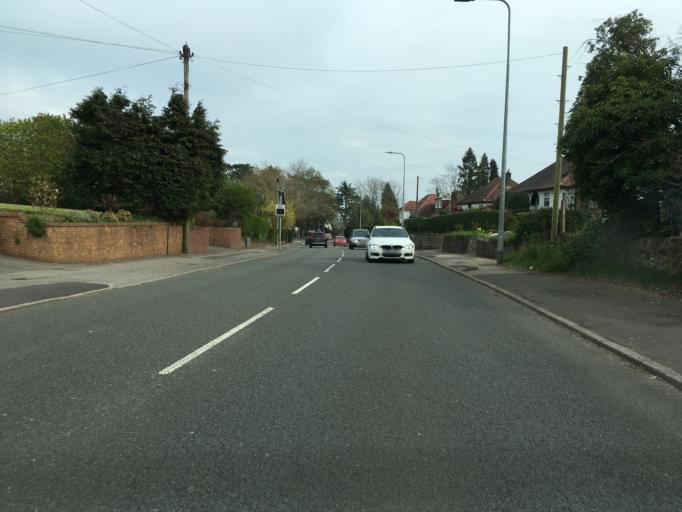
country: GB
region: Wales
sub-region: Cardiff
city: Radyr
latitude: 51.5290
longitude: -3.2211
